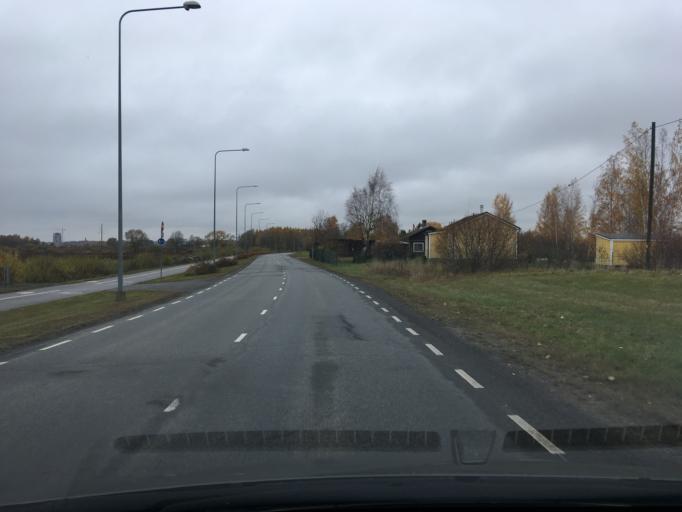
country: EE
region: Tartu
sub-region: Tartu linn
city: Tartu
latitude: 58.3617
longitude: 26.7596
